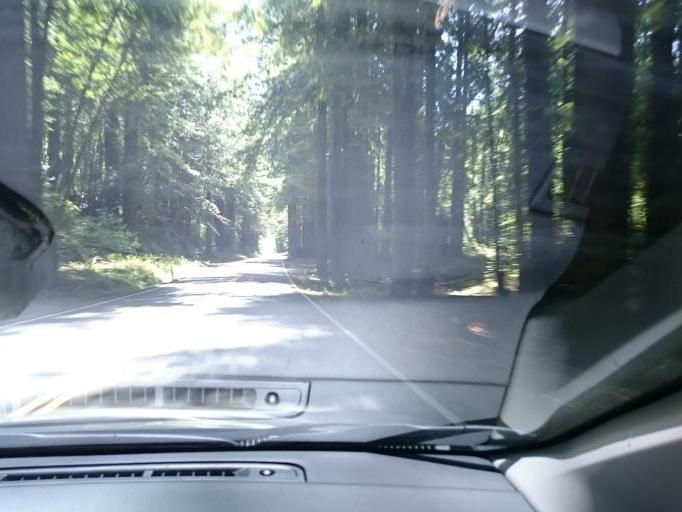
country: US
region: California
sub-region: Mendocino County
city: Fort Bragg
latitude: 39.1666
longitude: -123.6594
